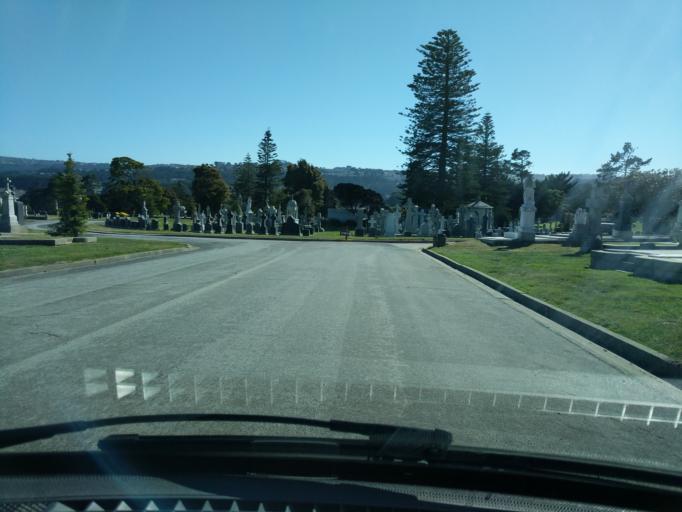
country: US
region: California
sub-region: San Mateo County
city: Colma
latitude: 37.6716
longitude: -122.4447
